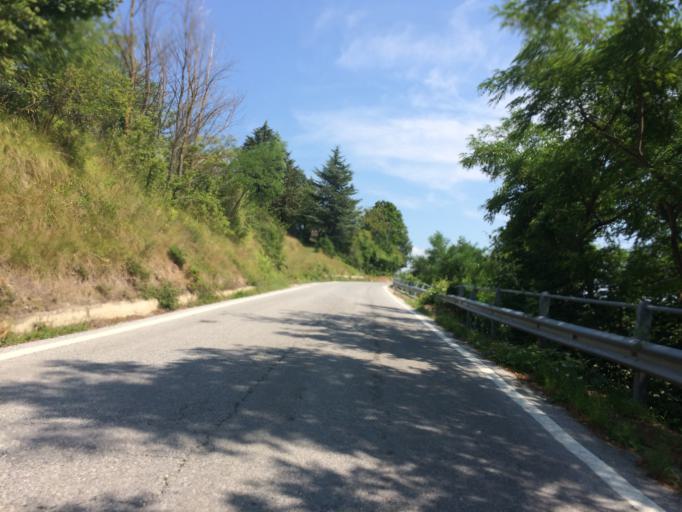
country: IT
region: Piedmont
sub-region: Provincia di Cuneo
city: Serravalle Langhe
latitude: 44.5592
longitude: 8.0483
